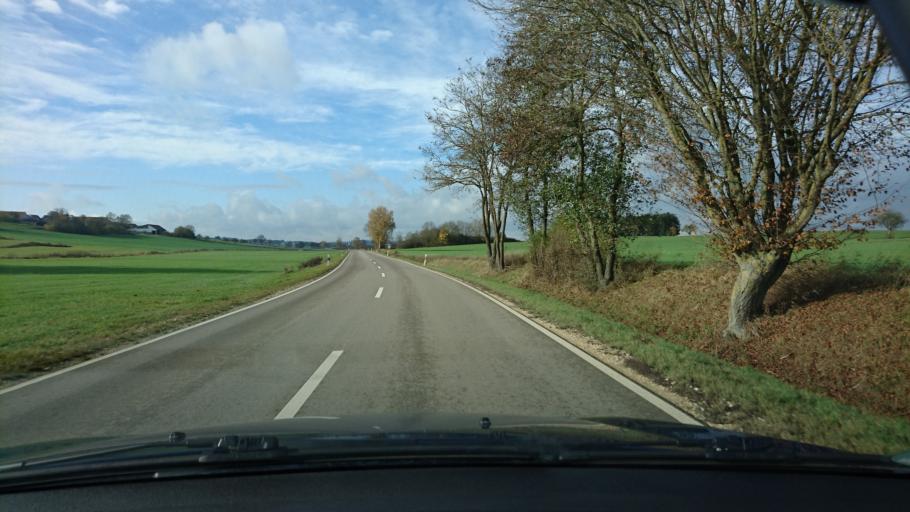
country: DE
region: Bavaria
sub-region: Swabia
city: Amerdingen
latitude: 48.7270
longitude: 10.5267
